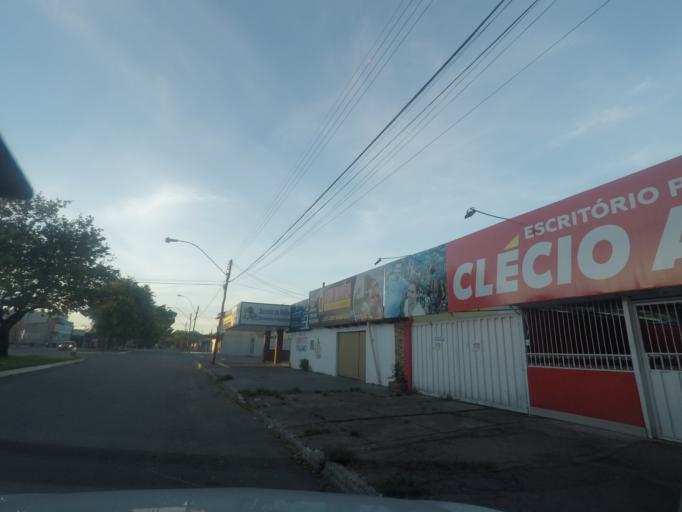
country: BR
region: Goias
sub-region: Goiania
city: Goiania
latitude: -16.6888
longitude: -49.3513
